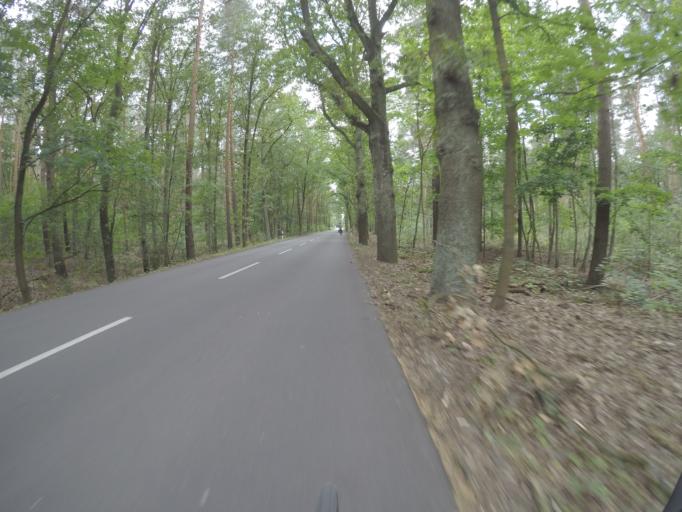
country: DE
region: Berlin
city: Heiligensee
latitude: 52.6242
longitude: 13.2515
